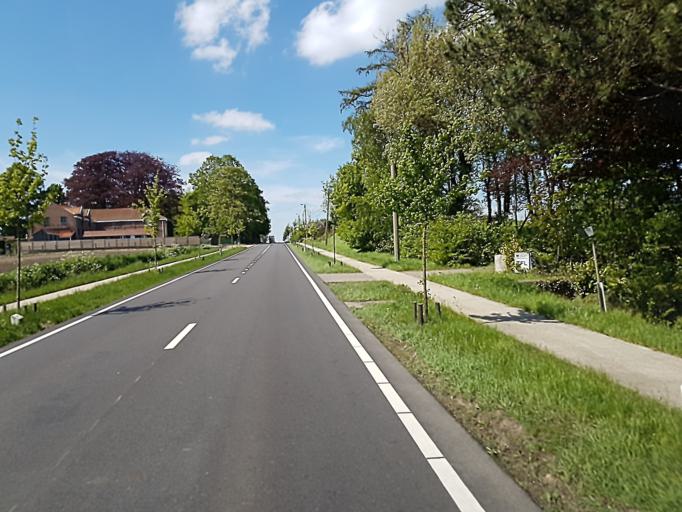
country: BE
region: Flanders
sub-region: Provincie Vlaams-Brabant
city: Glabbeek-Zuurbemde
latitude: 50.8502
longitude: 4.9054
